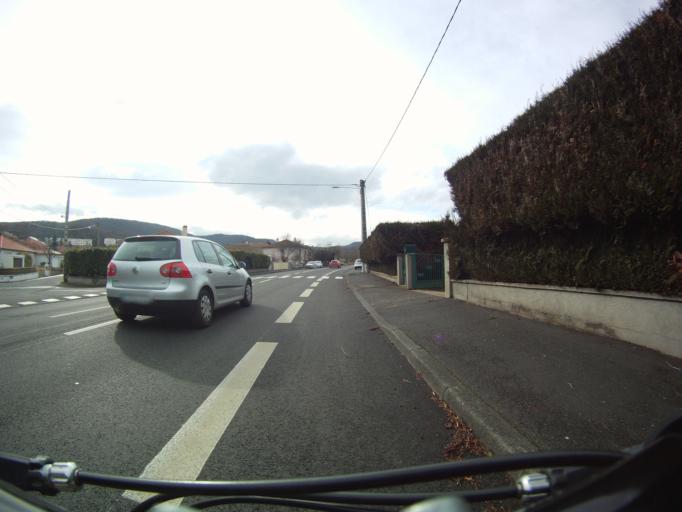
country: FR
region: Auvergne
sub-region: Departement du Puy-de-Dome
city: Romagnat
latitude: 45.7392
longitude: 3.1060
